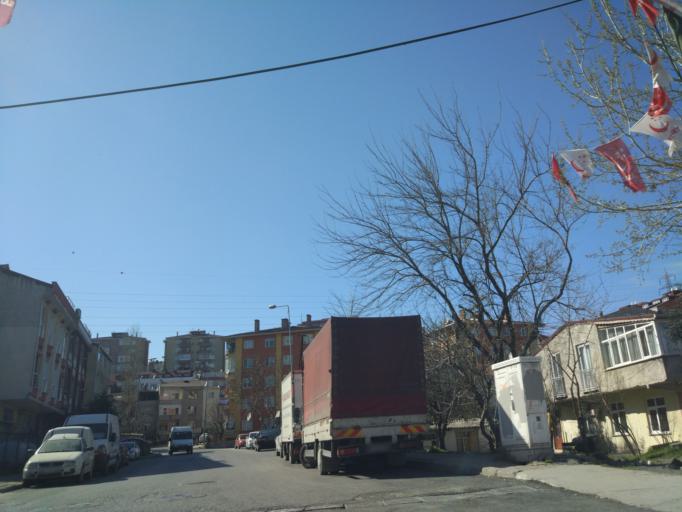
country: TR
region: Istanbul
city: Mahmutbey
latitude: 41.0202
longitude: 28.8051
